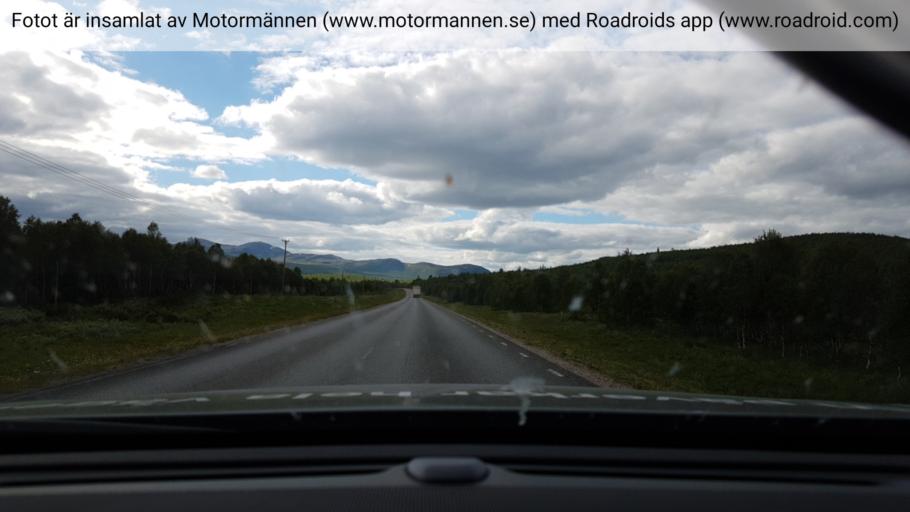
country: SE
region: Norrbotten
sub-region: Arjeplogs Kommun
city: Arjeplog
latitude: 66.3089
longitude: 17.1337
